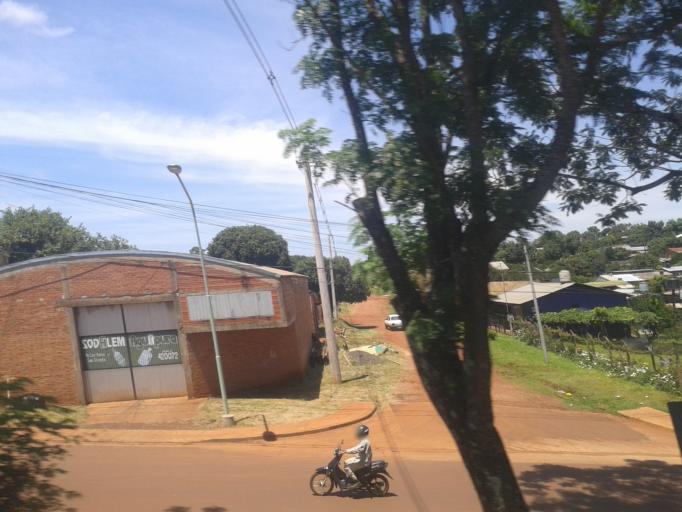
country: AR
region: Misiones
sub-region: Departamento de Leandro N. Alem
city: Leandro N. Alem
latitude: -27.6050
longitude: -55.3380
